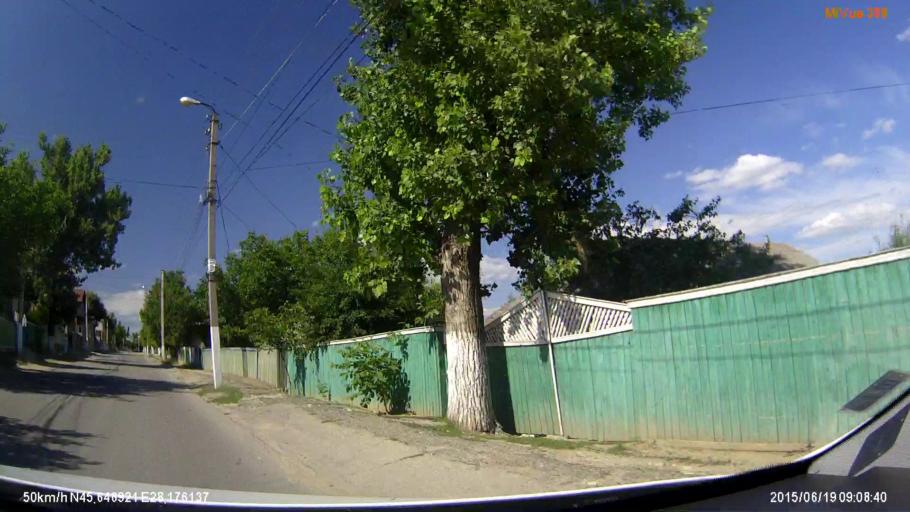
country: RO
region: Galati
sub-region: Comuna Frumusita
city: Frumusita
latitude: 45.6468
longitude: 28.1761
